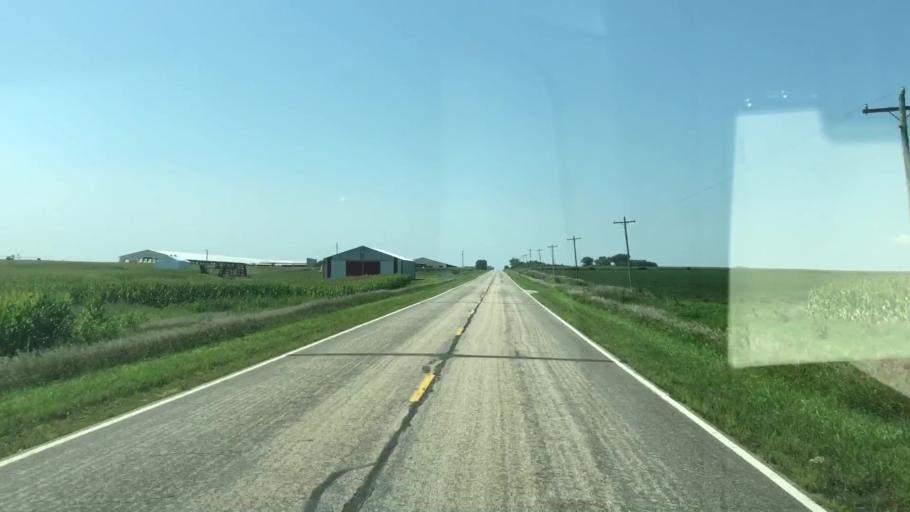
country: US
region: Iowa
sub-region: O'Brien County
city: Sanborn
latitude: 43.2728
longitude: -95.6886
